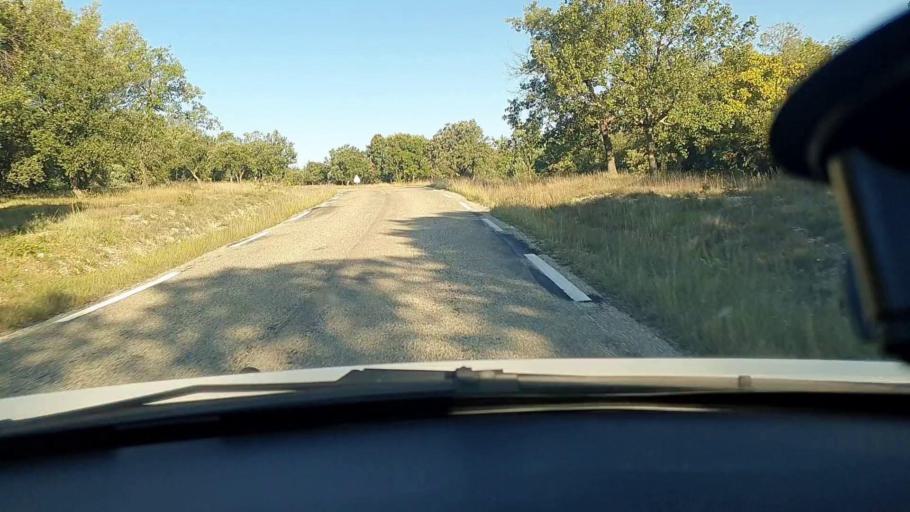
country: FR
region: Languedoc-Roussillon
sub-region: Departement du Gard
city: Barjac
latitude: 44.1666
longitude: 4.3286
